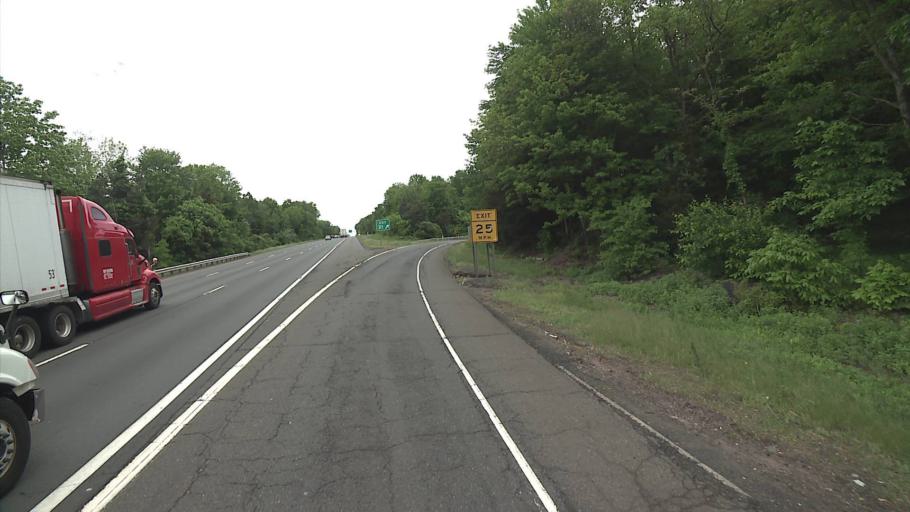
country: US
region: Connecticut
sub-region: Middlesex County
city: Cromwell
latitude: 41.6044
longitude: -72.7036
